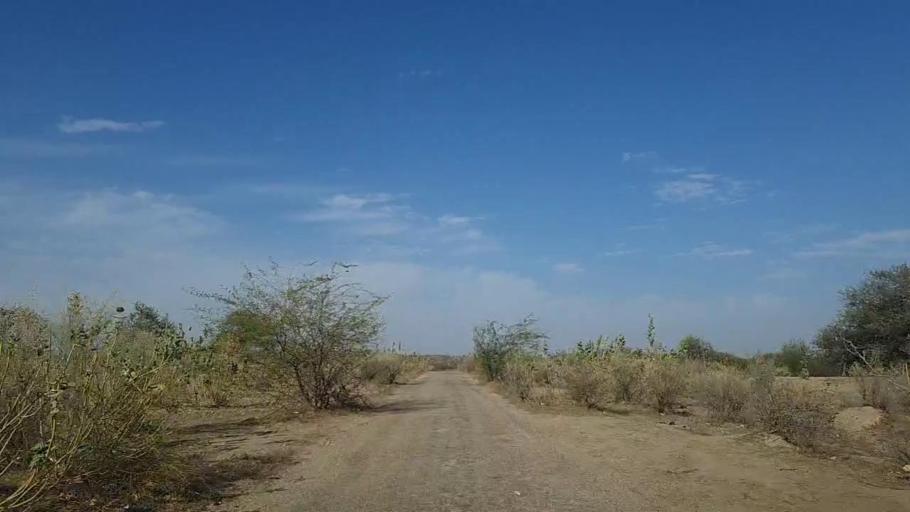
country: PK
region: Sindh
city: Naukot
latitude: 24.8474
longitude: 69.5335
